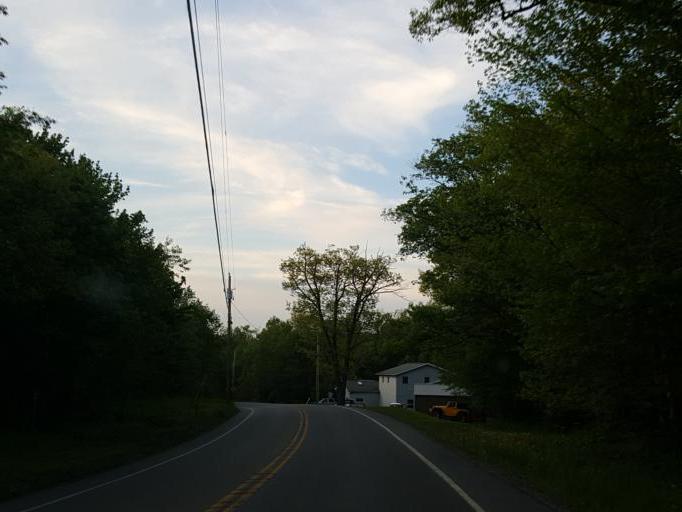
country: US
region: Pennsylvania
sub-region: Cambria County
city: Gallitzin
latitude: 40.5222
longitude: -78.5307
